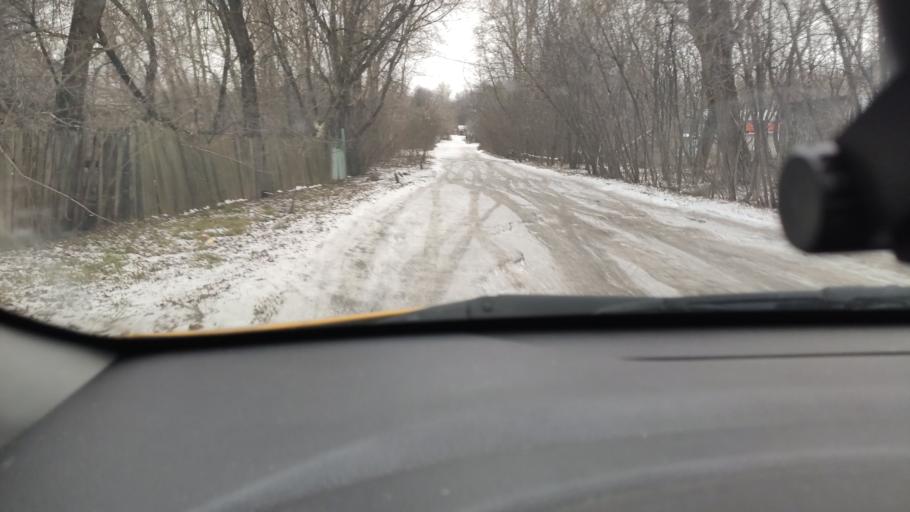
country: RU
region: Moscow
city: Chertanovo Yuzhnoye
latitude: 55.5950
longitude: 37.5819
